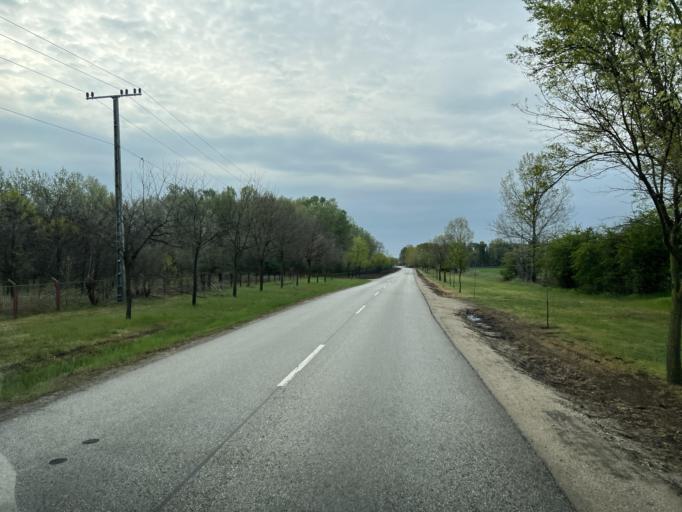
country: HU
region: Pest
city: Ujhartyan
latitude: 47.2395
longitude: 19.4417
